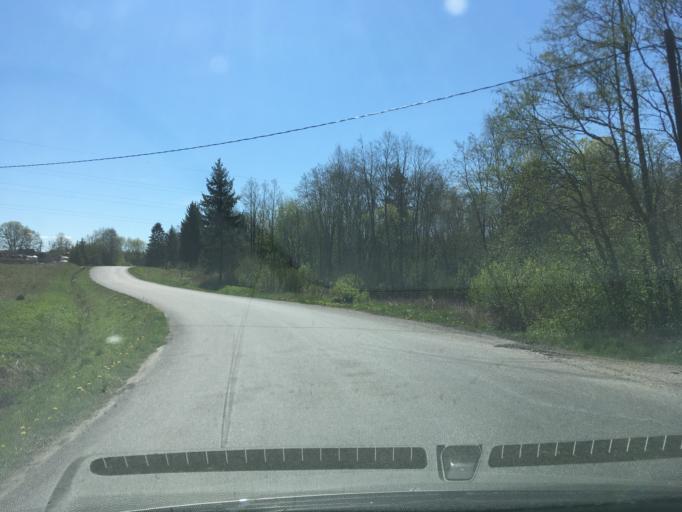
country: EE
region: Harju
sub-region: Raasiku vald
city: Arukula
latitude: 59.3834
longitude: 25.0771
